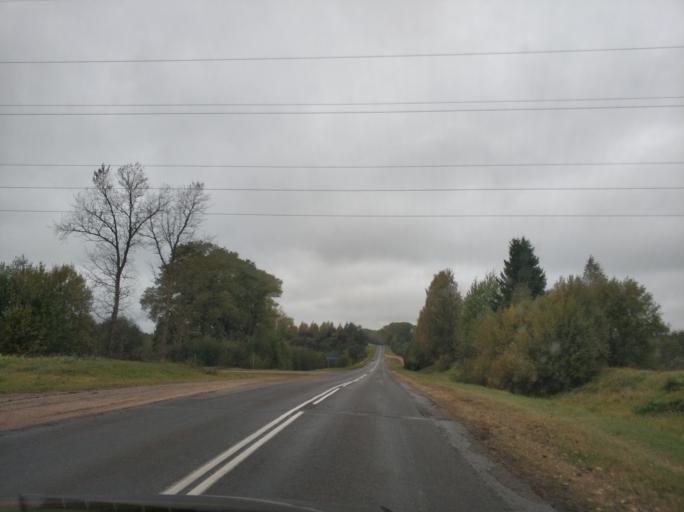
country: BY
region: Vitebsk
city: Polatsk
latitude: 55.4405
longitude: 28.9576
